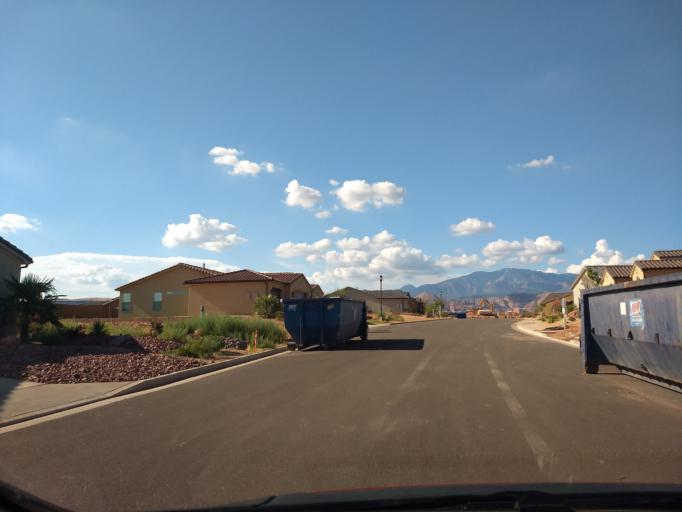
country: US
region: Utah
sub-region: Washington County
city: Washington
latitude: 37.1437
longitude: -113.5162
